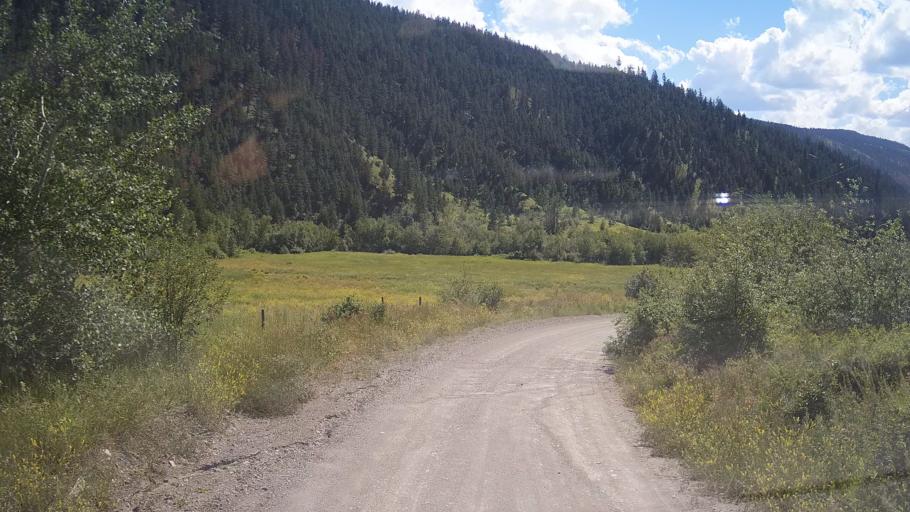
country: CA
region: British Columbia
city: Lillooet
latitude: 51.2438
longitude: -122.0378
